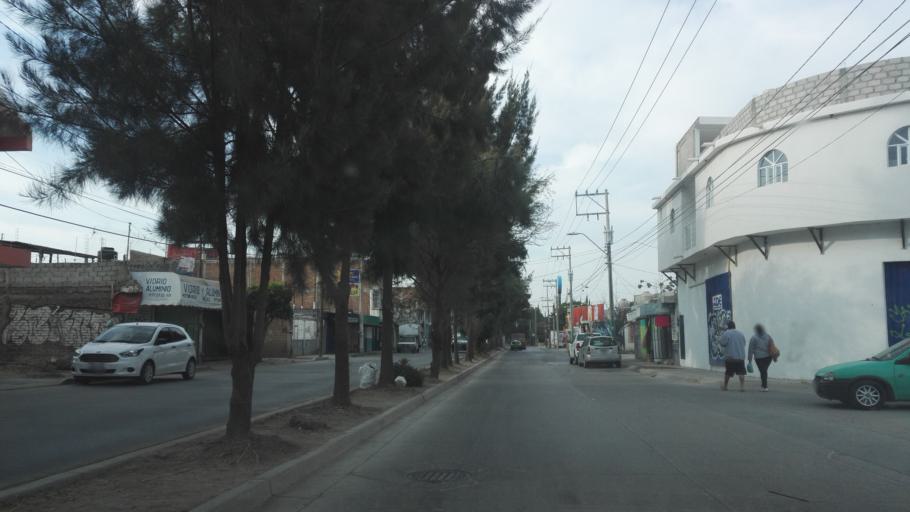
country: MX
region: Guanajuato
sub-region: Leon
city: Fraccionamiento Paraiso Real
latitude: 21.0985
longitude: -101.6029
